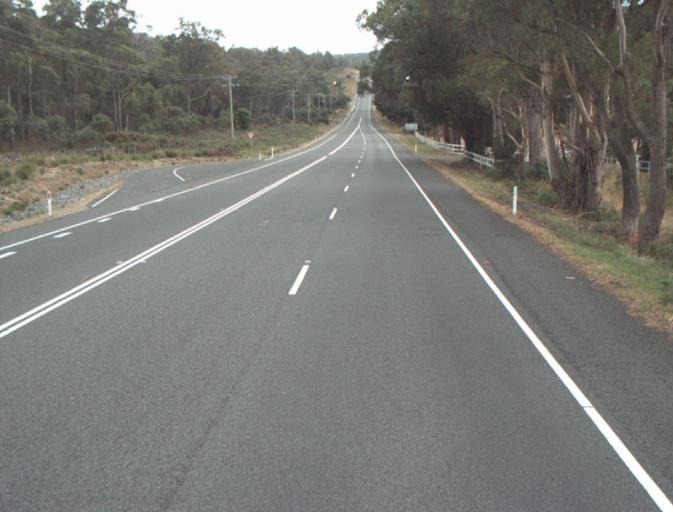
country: AU
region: Tasmania
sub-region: Launceston
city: Mayfield
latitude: -41.2759
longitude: 147.0369
